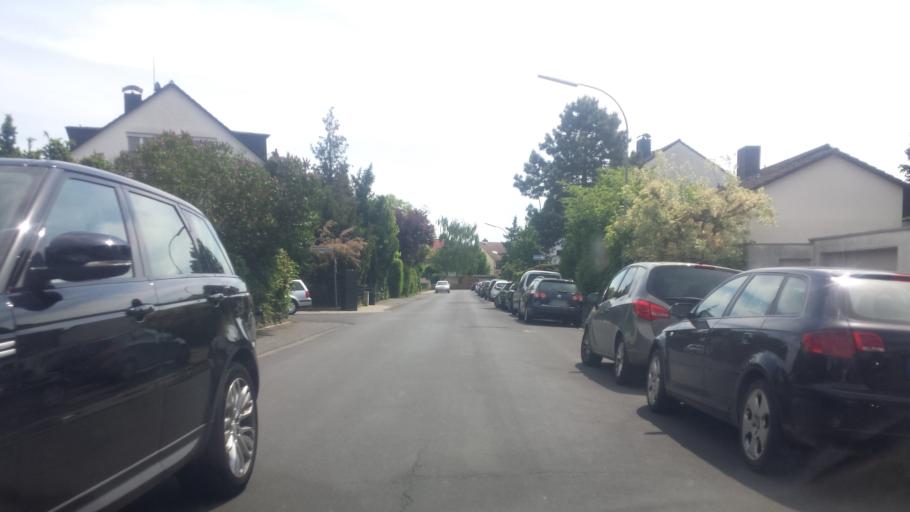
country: DE
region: Hesse
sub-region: Regierungsbezirk Darmstadt
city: Karben
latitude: 50.2092
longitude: 8.7563
